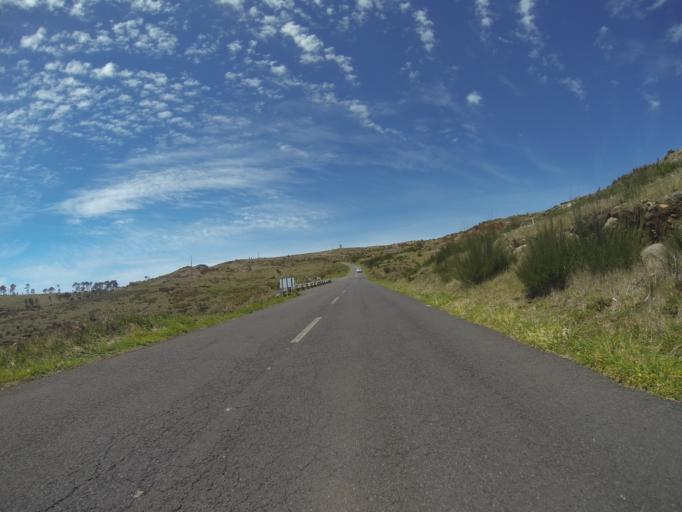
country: PT
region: Madeira
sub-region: Funchal
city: Nossa Senhora do Monte
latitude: 32.7181
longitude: -16.9132
